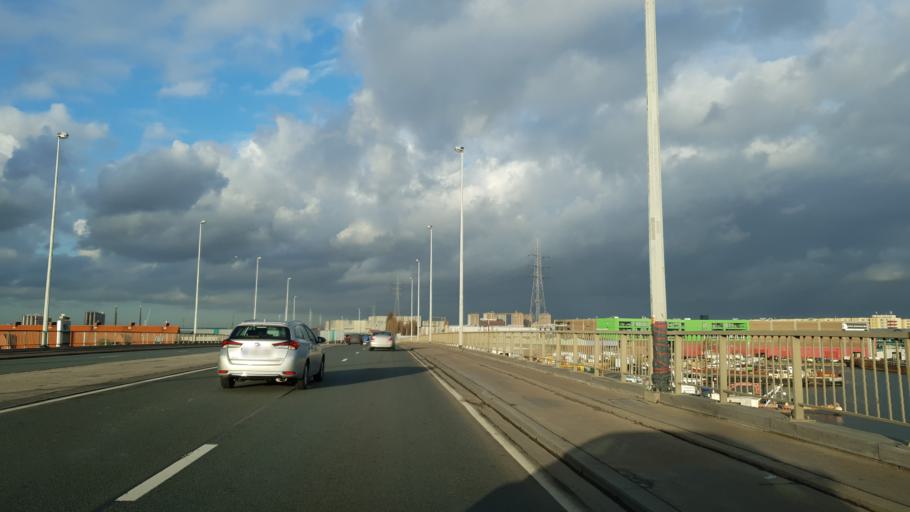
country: BE
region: Flanders
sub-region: Provincie Antwerpen
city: Antwerpen
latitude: 51.2415
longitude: 4.4123
